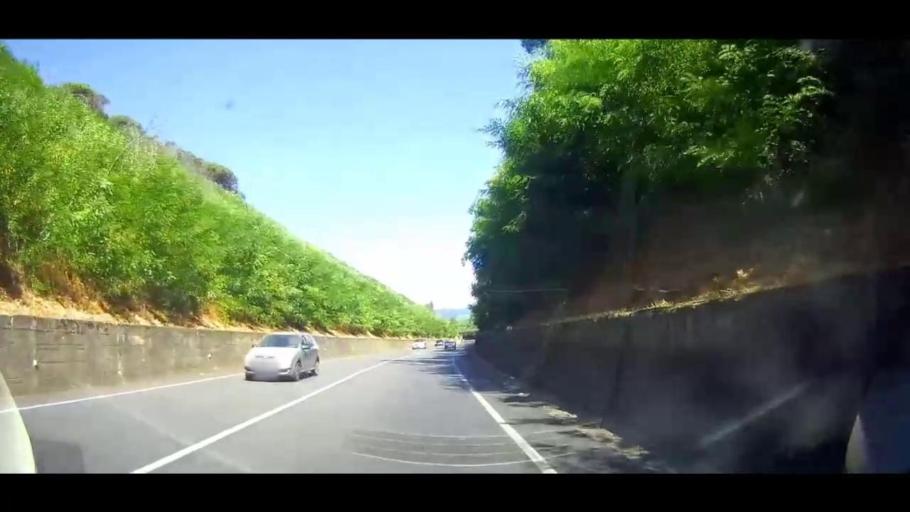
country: IT
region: Calabria
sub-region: Provincia di Cosenza
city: Zumpano
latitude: 39.2986
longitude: 16.2929
